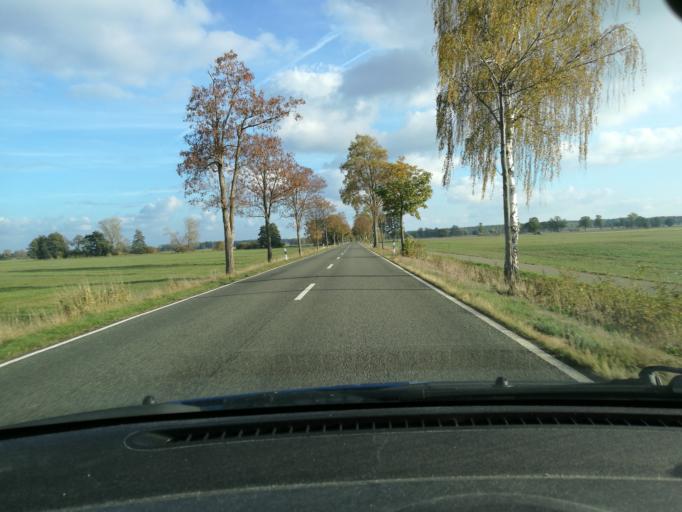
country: DE
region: Lower Saxony
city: Prezelle
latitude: 52.9038
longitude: 11.4195
